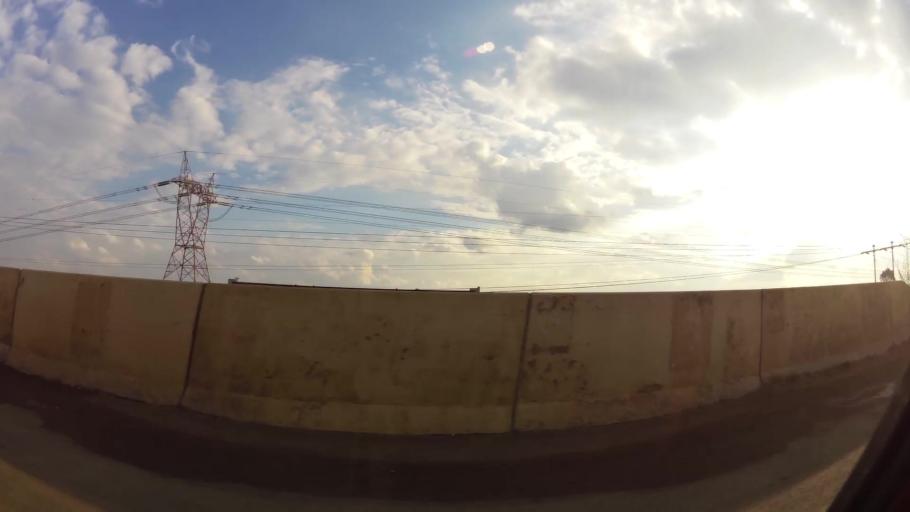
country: ZA
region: Gauteng
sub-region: Sedibeng District Municipality
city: Vereeniging
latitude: -26.6370
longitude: 27.8708
